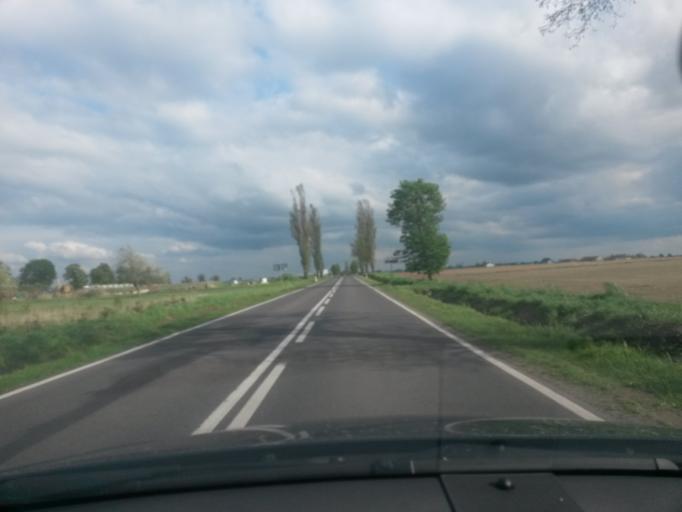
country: PL
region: Masovian Voivodeship
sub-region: Powiat sierpecki
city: Zawidz
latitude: 52.8465
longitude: 19.8394
